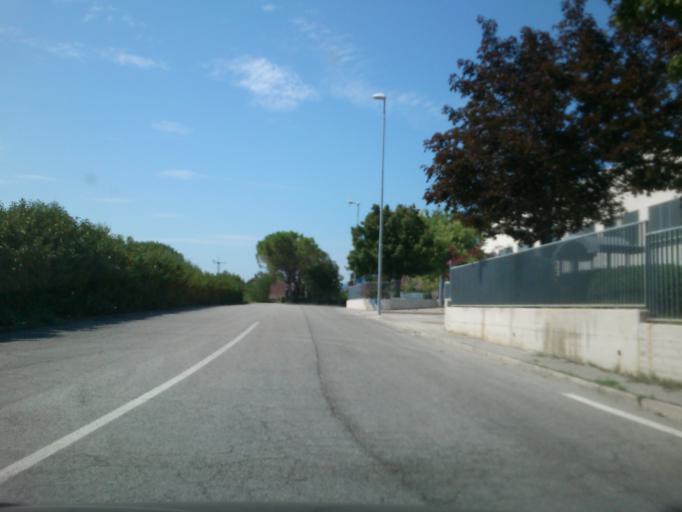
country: IT
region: The Marches
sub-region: Provincia di Pesaro e Urbino
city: Lucrezia
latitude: 43.7649
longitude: 12.9531
